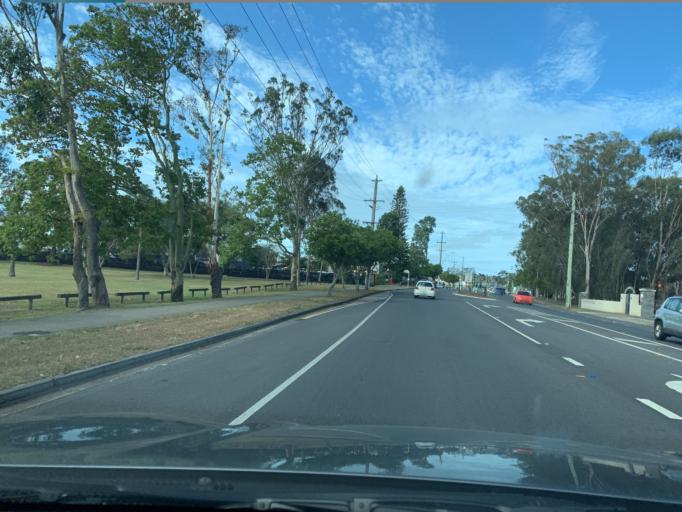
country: AU
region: Queensland
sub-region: Brisbane
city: Wynnum West
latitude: -27.4702
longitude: 153.1496
